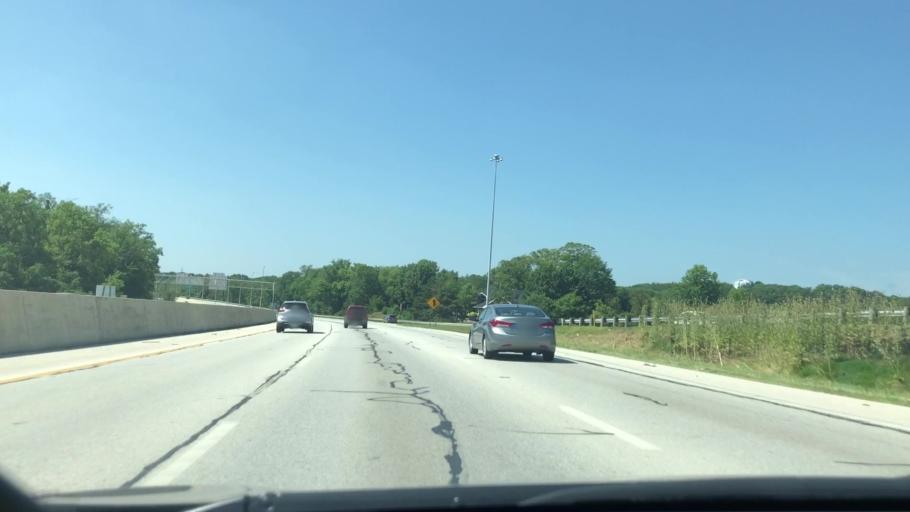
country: US
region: Ohio
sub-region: Summit County
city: Fairlawn
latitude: 41.1003
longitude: -81.5883
